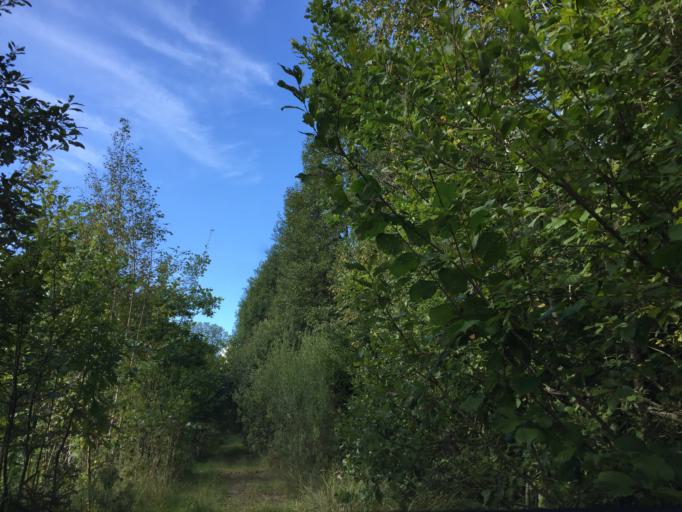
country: LV
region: Kuldigas Rajons
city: Kuldiga
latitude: 56.9788
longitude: 21.9018
